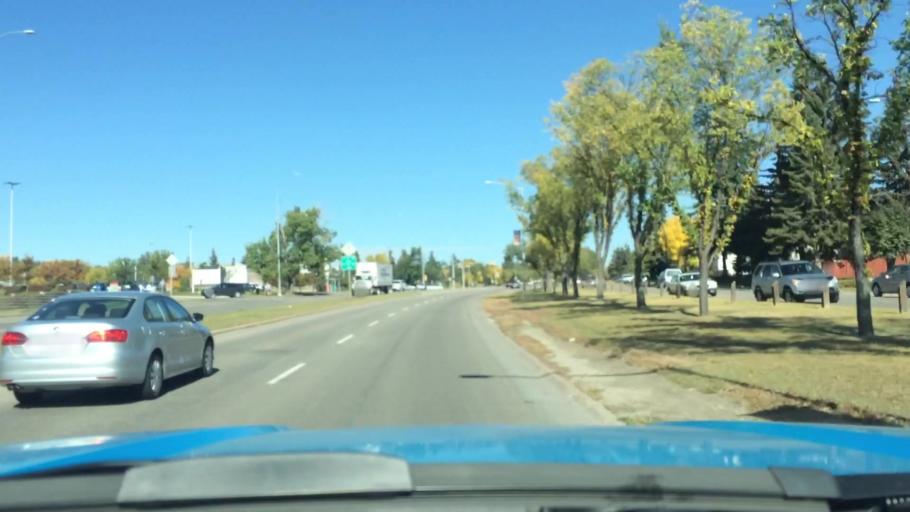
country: CA
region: Alberta
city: Calgary
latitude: 51.1162
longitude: -114.0679
